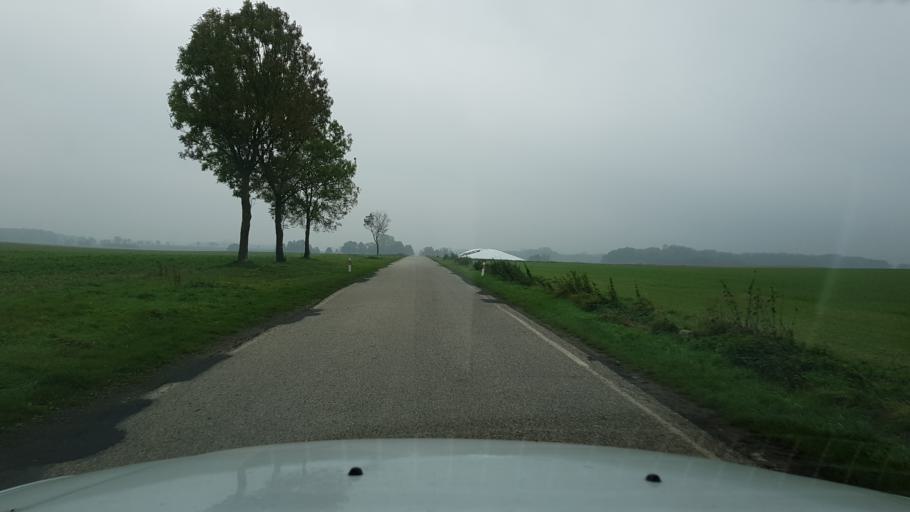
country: PL
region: West Pomeranian Voivodeship
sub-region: Powiat stargardzki
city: Dolice
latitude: 53.1689
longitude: 15.2223
